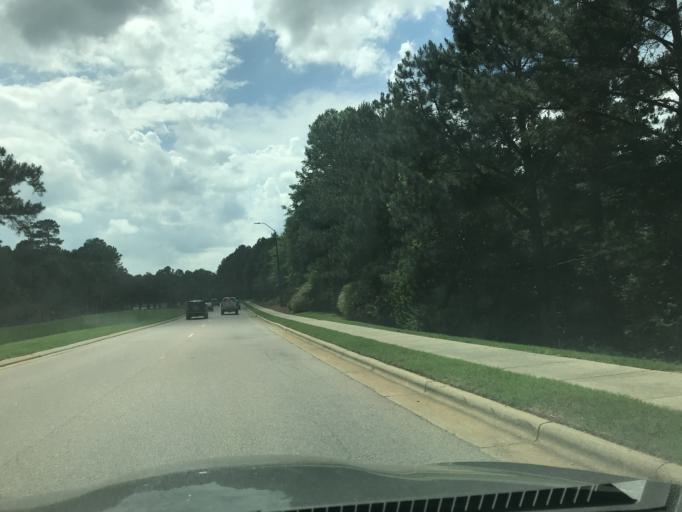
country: US
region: North Carolina
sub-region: Wake County
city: Wake Forest
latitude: 35.9397
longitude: -78.5667
